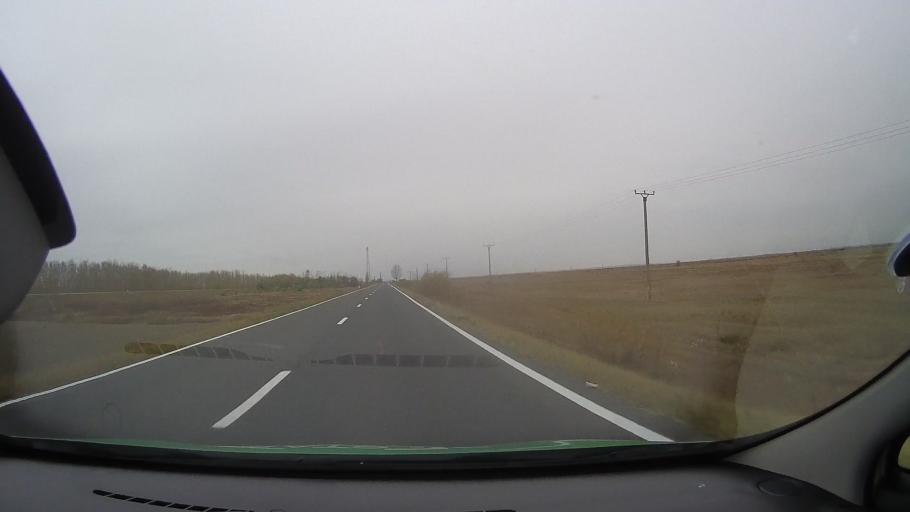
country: RO
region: Ialomita
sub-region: Comuna Giurgeni
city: Giurgeni
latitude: 44.7282
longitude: 27.8540
